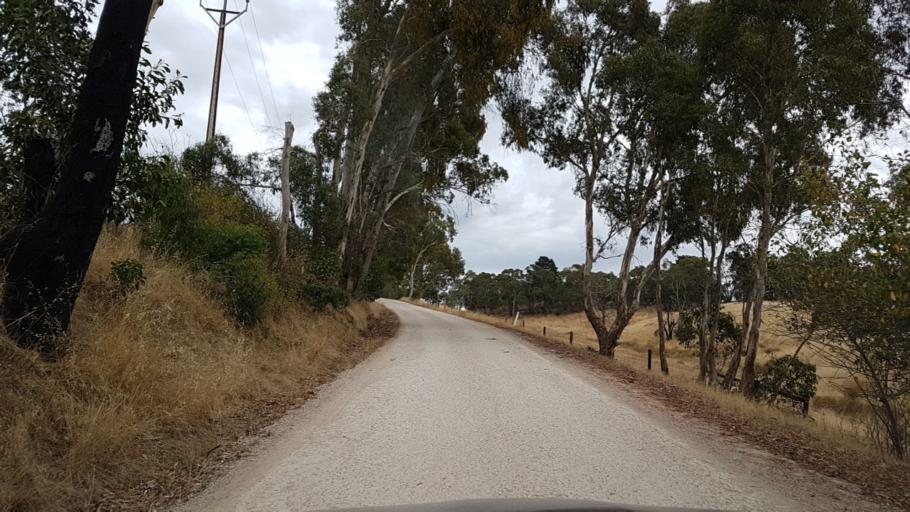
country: AU
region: South Australia
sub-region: Adelaide Hills
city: Gumeracha
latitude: -34.8043
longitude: 138.8089
